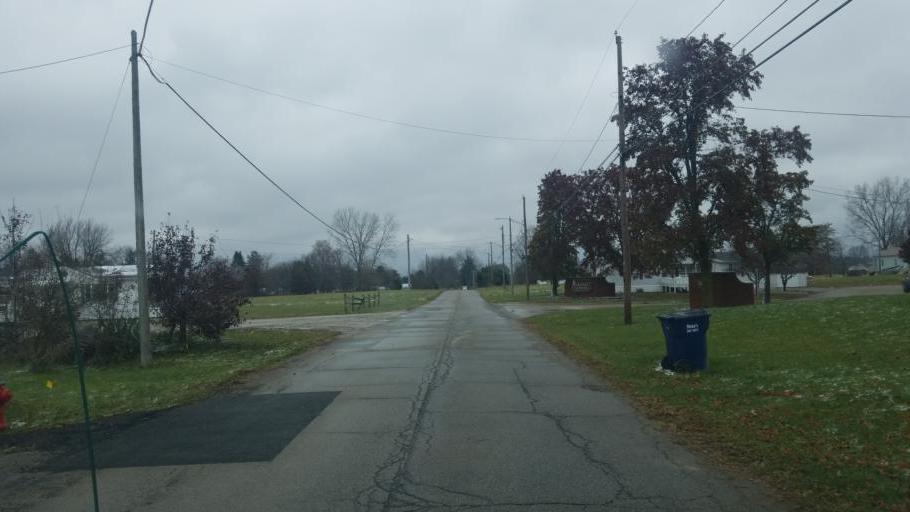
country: US
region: Ohio
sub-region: Richland County
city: Shelby
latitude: 40.8926
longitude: -82.6545
